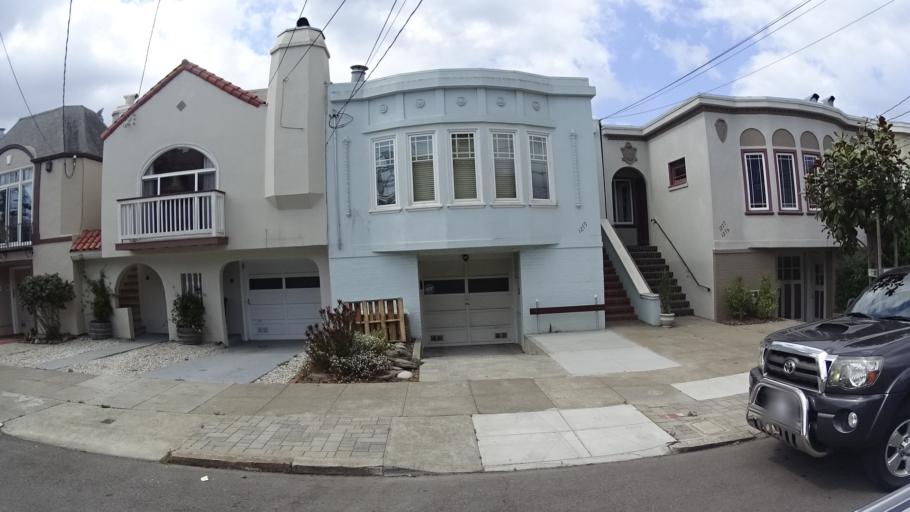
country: US
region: California
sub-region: San Mateo County
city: Daly City
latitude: 37.7633
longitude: -122.4943
